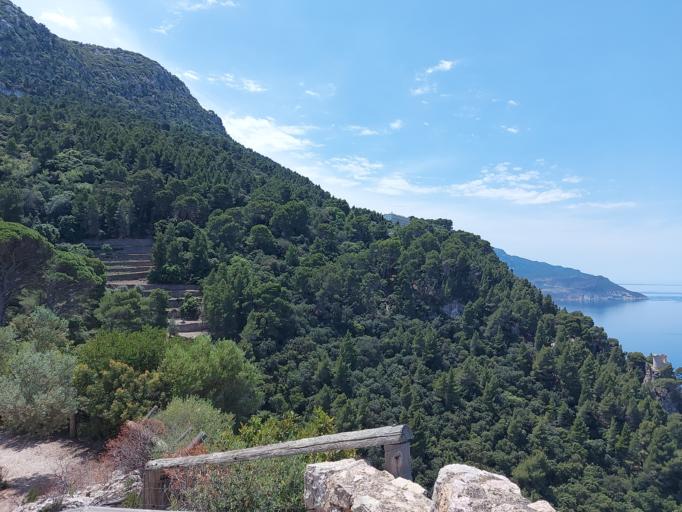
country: ES
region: Balearic Islands
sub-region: Illes Balears
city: Valldemossa
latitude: 39.7394
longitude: 2.6167
